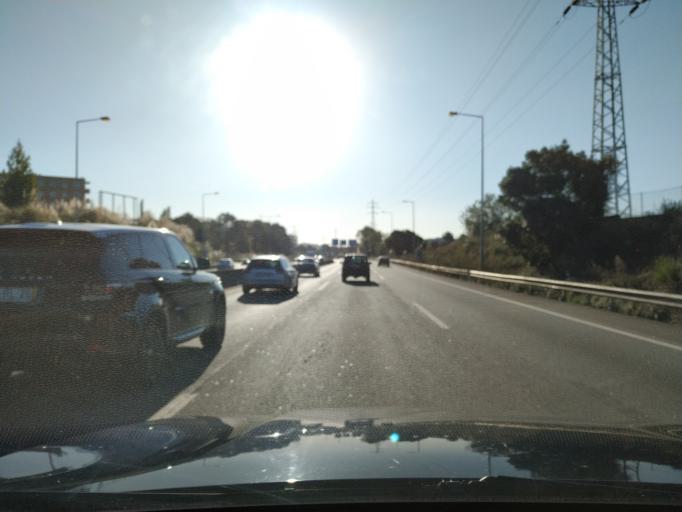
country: PT
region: Porto
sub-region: Vila Nova de Gaia
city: Canidelo
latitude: 41.1183
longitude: -8.6332
